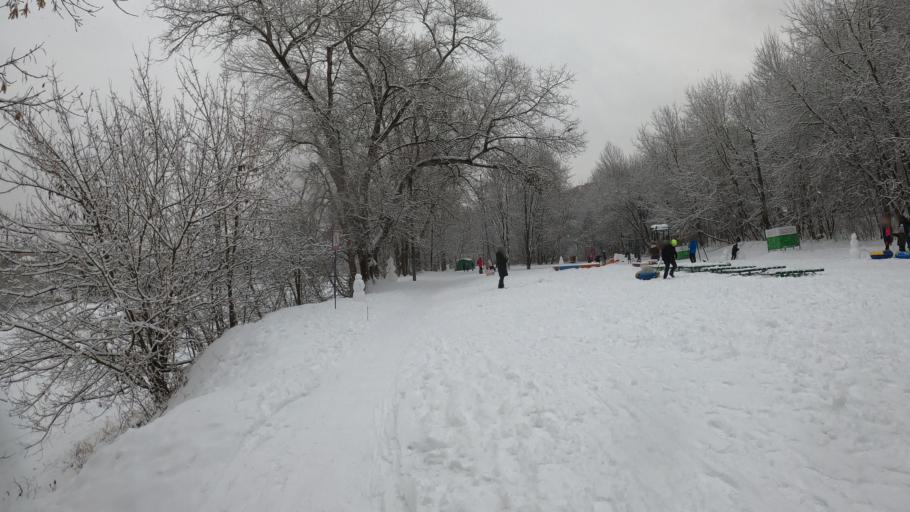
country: RU
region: Moskovskaya
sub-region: Podol'skiy Rayon
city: Podol'sk
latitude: 55.4355
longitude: 37.5304
